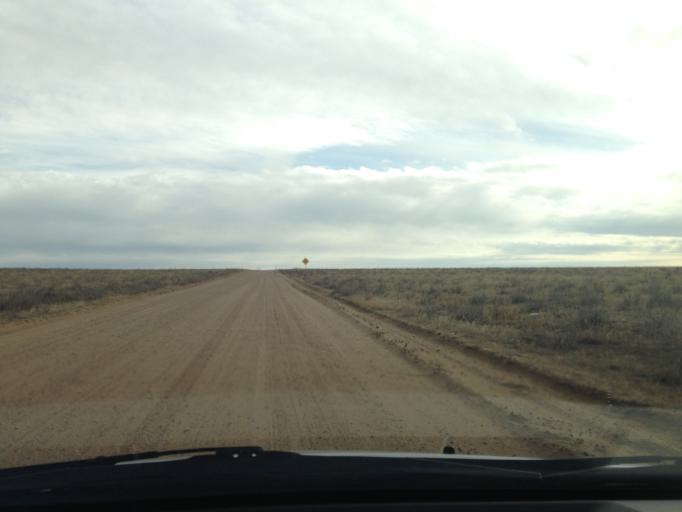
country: US
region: Colorado
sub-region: Weld County
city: Keenesburg
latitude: 40.2492
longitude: -104.2068
